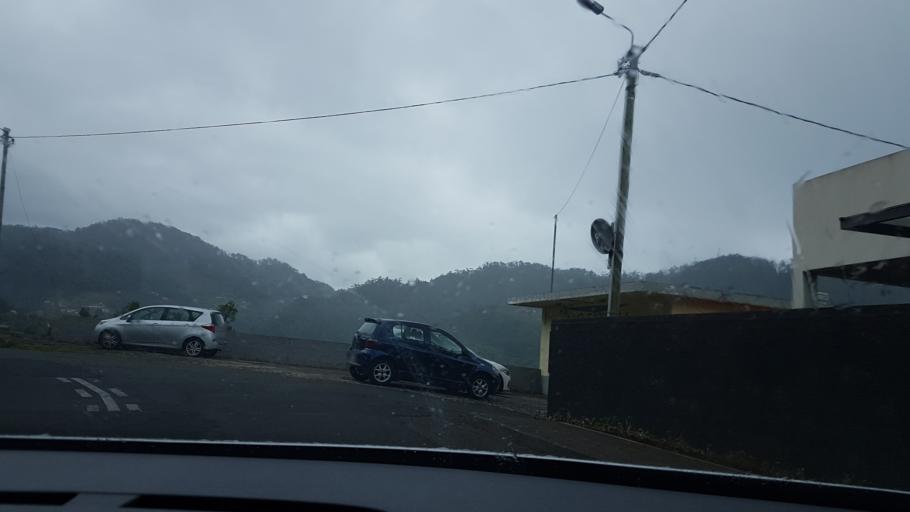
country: PT
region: Madeira
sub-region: Santa Cruz
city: Santa Cruz
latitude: 32.7317
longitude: -16.8111
